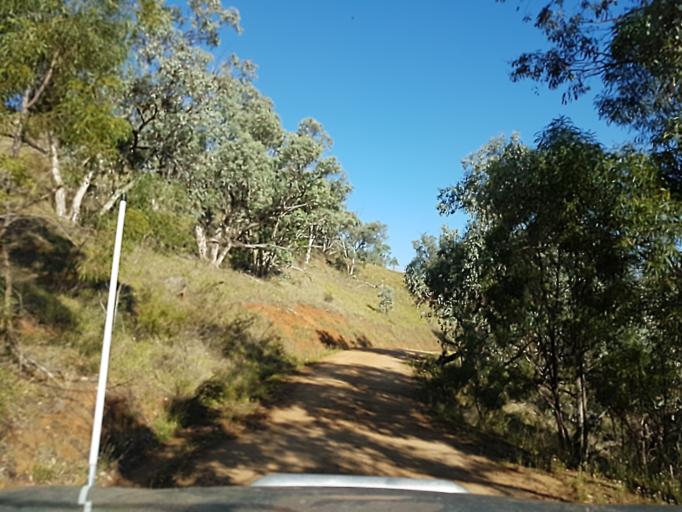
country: AU
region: New South Wales
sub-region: Snowy River
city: Jindabyne
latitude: -36.9489
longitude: 148.3493
